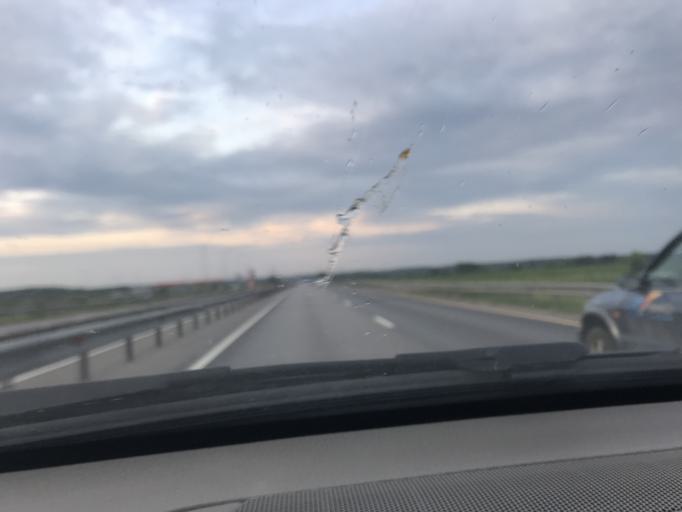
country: RU
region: Kaluga
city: Obninsk
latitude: 55.0359
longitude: 36.5863
